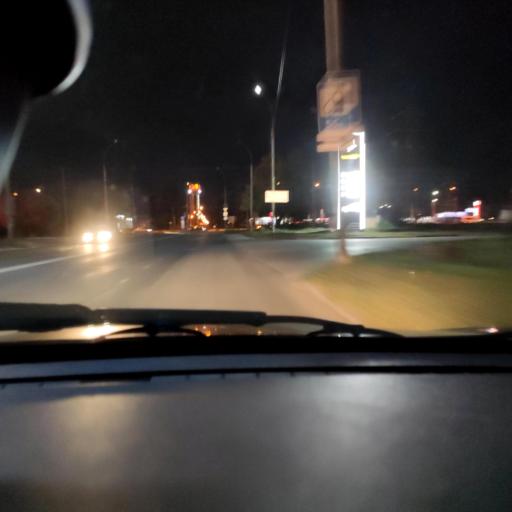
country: RU
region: Samara
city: Tol'yatti
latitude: 53.5490
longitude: 49.3176
